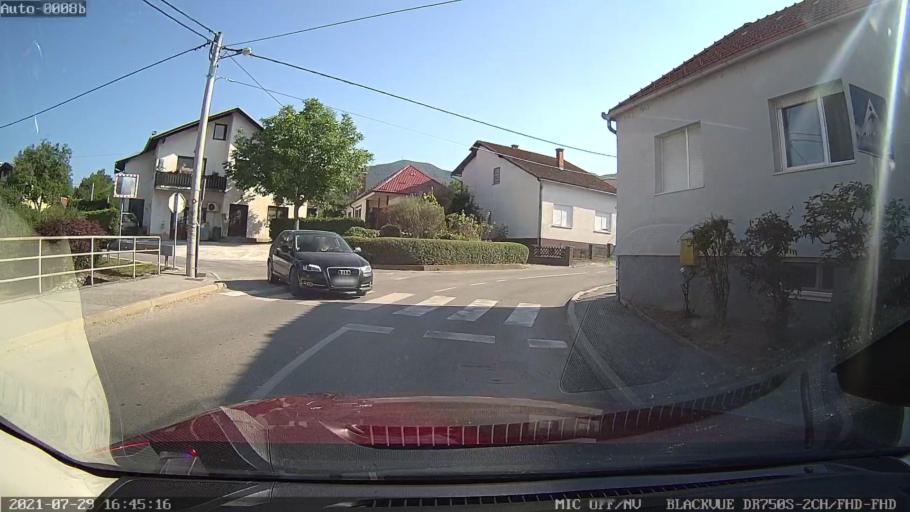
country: HR
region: Varazdinska
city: Ivanec
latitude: 46.2211
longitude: 16.1253
